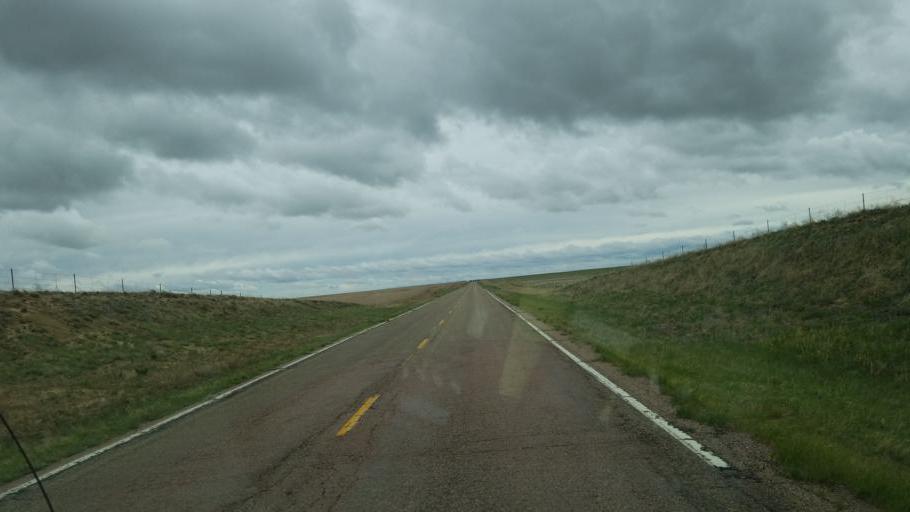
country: US
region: Colorado
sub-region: Lincoln County
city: Hugo
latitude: 38.8515
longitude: -103.6480
